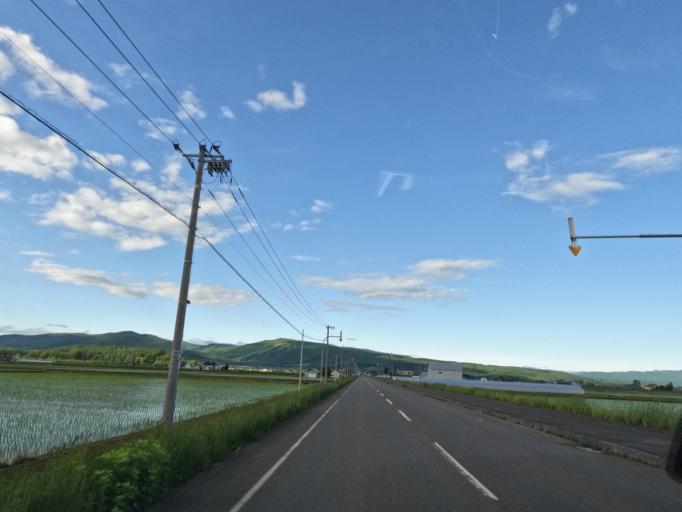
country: JP
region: Hokkaido
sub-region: Asahikawa-shi
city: Asahikawa
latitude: 43.8900
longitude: 142.4656
